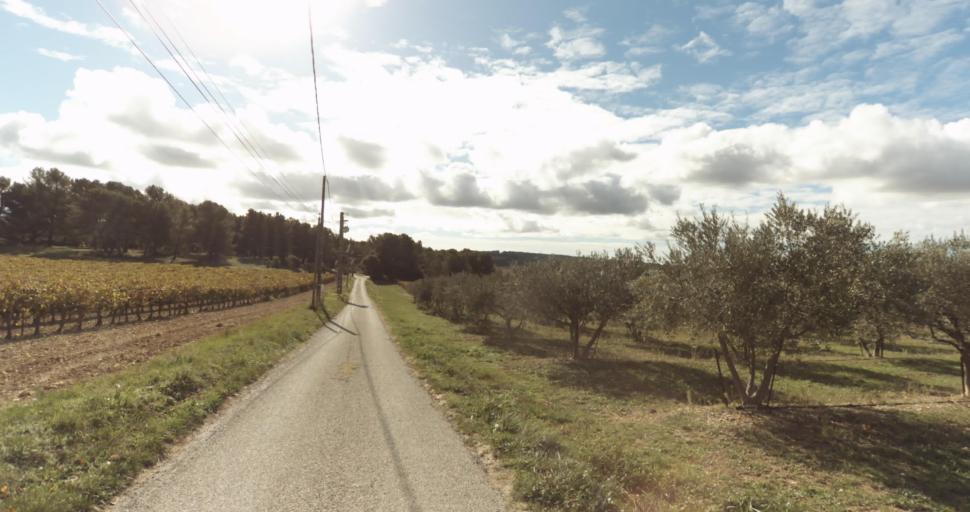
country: FR
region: Provence-Alpes-Cote d'Azur
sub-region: Departement des Bouches-du-Rhone
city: Venelles
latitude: 43.5924
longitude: 5.5003
